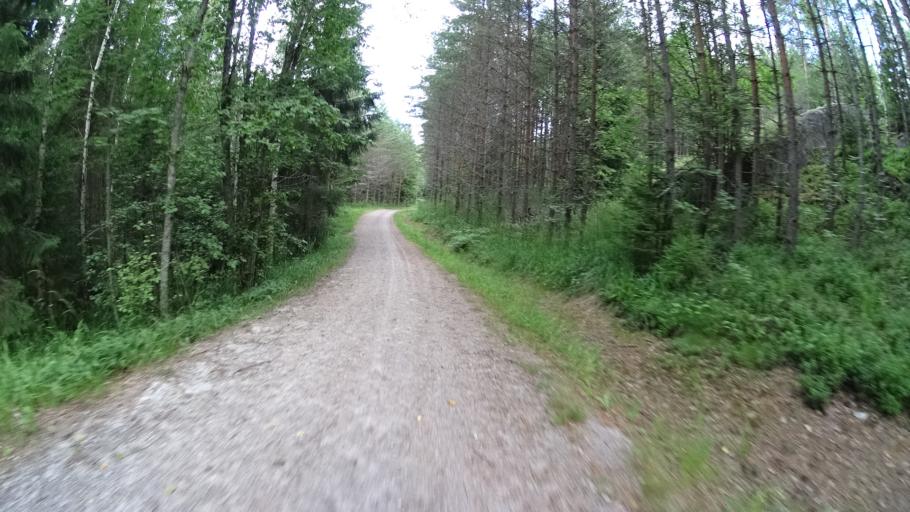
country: FI
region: Uusimaa
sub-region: Helsinki
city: Espoo
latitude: 60.2749
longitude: 24.6197
